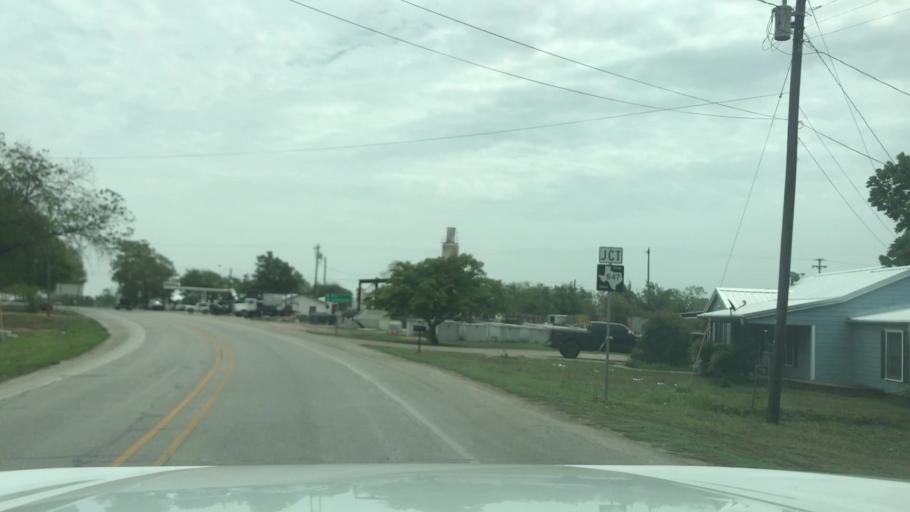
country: US
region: Texas
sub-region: Erath County
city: Dublin
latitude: 32.0831
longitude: -98.3341
